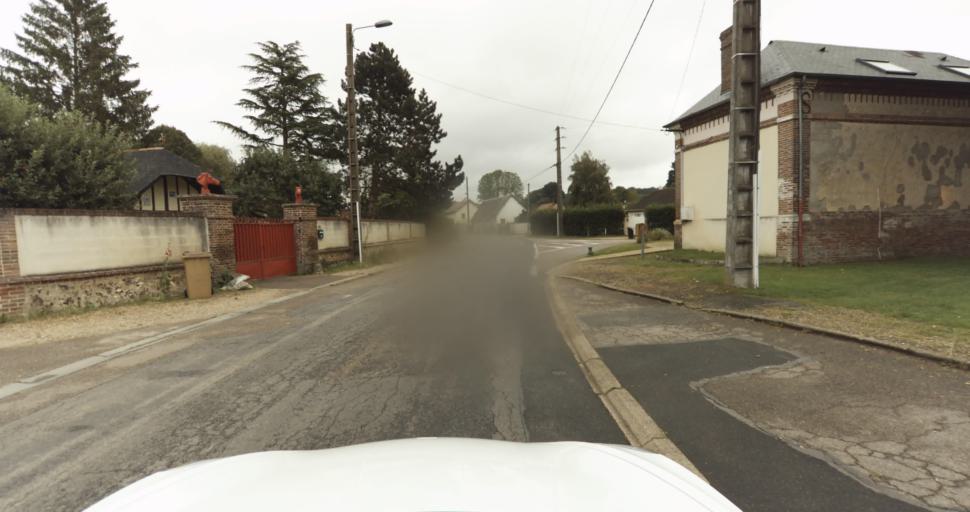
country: FR
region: Haute-Normandie
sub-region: Departement de l'Eure
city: Normanville
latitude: 49.0975
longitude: 1.1168
